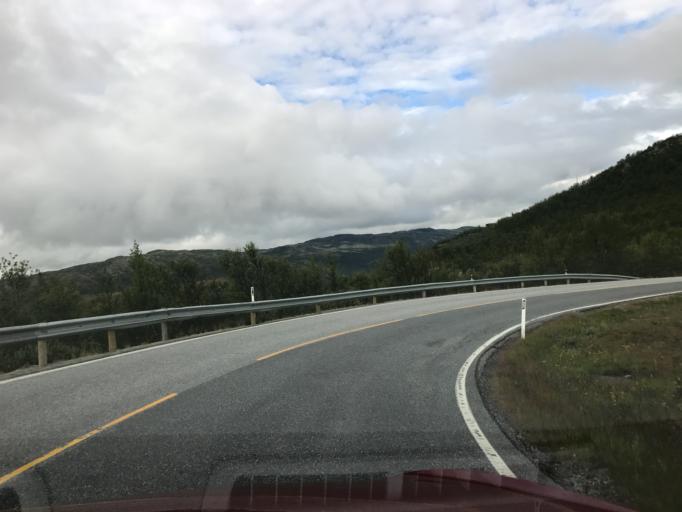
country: NO
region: Buskerud
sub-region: Al
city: Al
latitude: 60.3330
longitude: 8.5018
